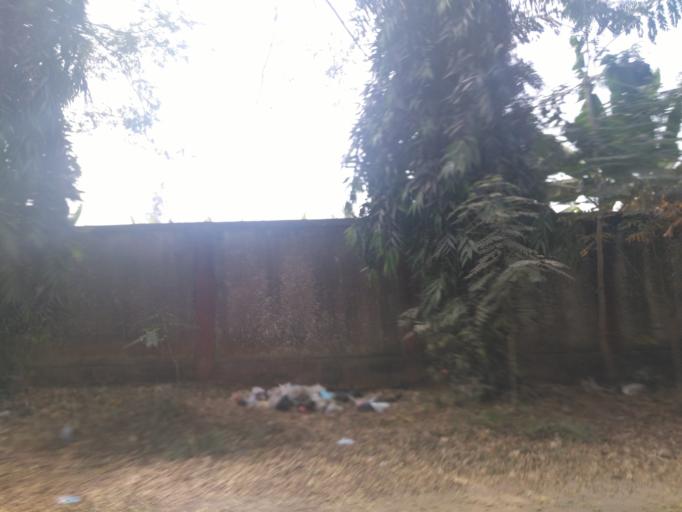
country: GH
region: Ashanti
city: Kumasi
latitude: 6.6833
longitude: -1.6265
